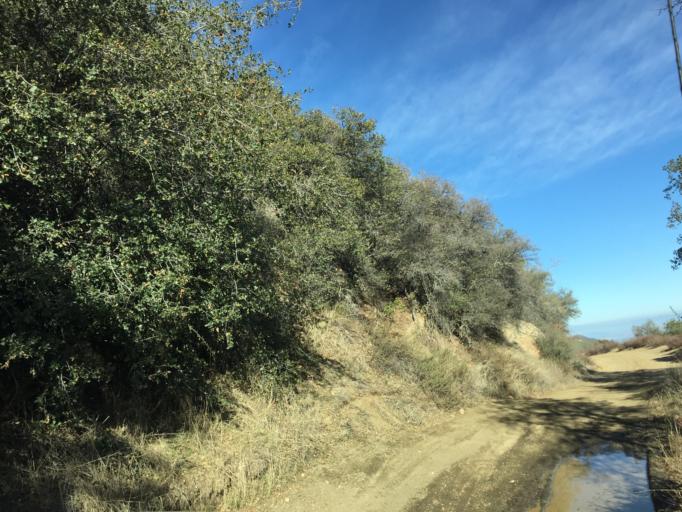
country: US
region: California
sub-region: Riverside County
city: Anza
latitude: 33.6141
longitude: -116.8058
